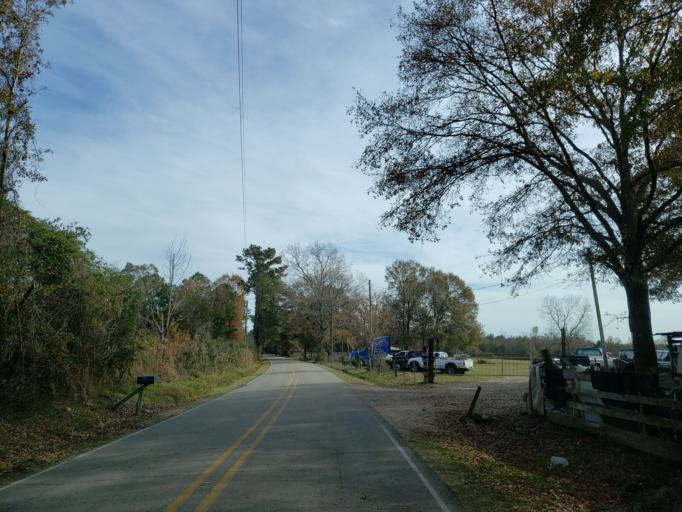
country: US
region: Mississippi
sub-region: Forrest County
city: Rawls Springs
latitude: 31.4007
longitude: -89.3943
